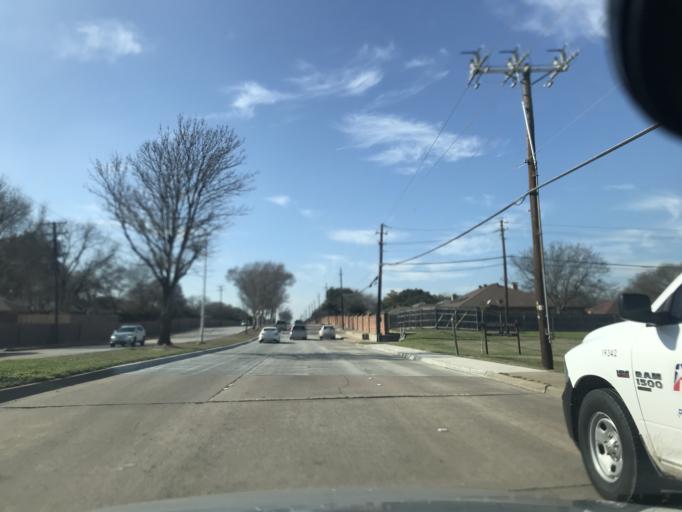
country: US
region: Texas
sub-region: Collin County
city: Plano
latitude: 33.0411
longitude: -96.7231
